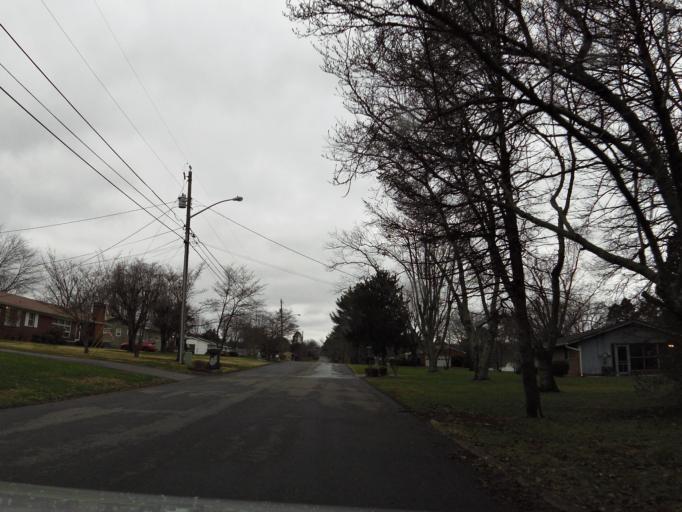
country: US
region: Tennessee
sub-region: Knox County
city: Knoxville
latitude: 35.9798
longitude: -84.0076
